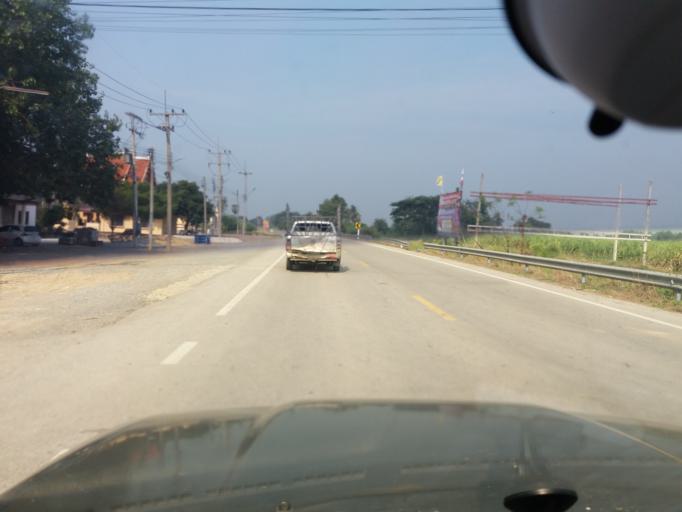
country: TH
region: Sing Buri
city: Bang Racham
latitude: 14.9026
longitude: 100.2672
